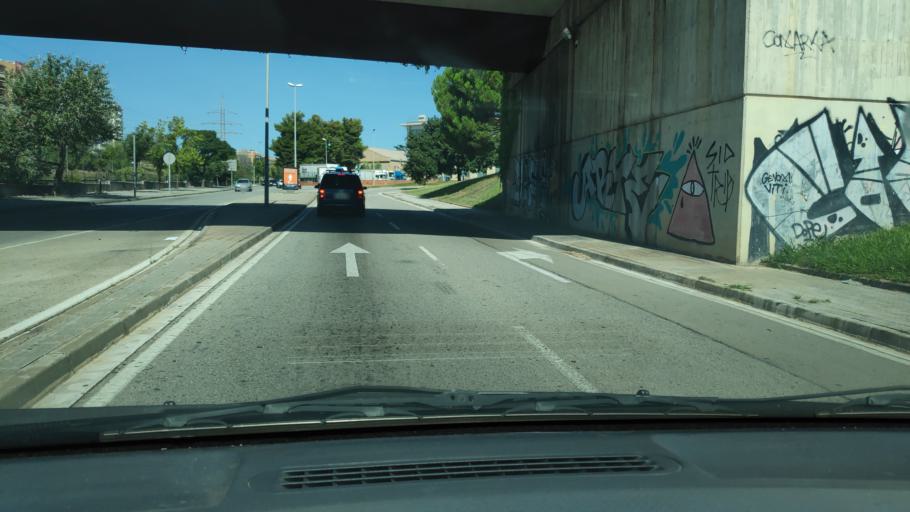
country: ES
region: Catalonia
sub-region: Provincia de Barcelona
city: Terrassa
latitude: 41.5541
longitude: 2.0378
